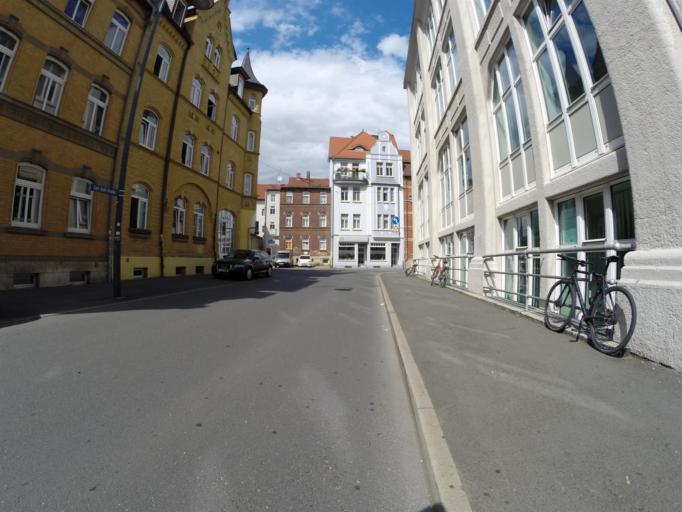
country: DE
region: Thuringia
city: Jena
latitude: 50.9291
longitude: 11.5811
